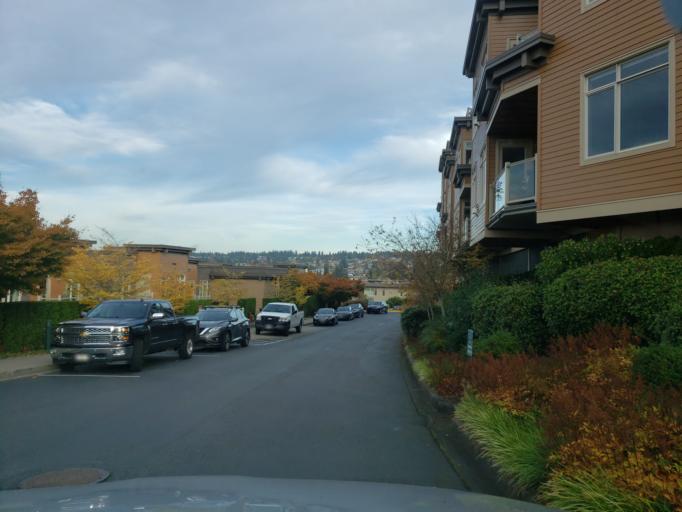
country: US
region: Washington
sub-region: Snohomish County
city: Woodway
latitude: 47.8044
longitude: -122.3907
